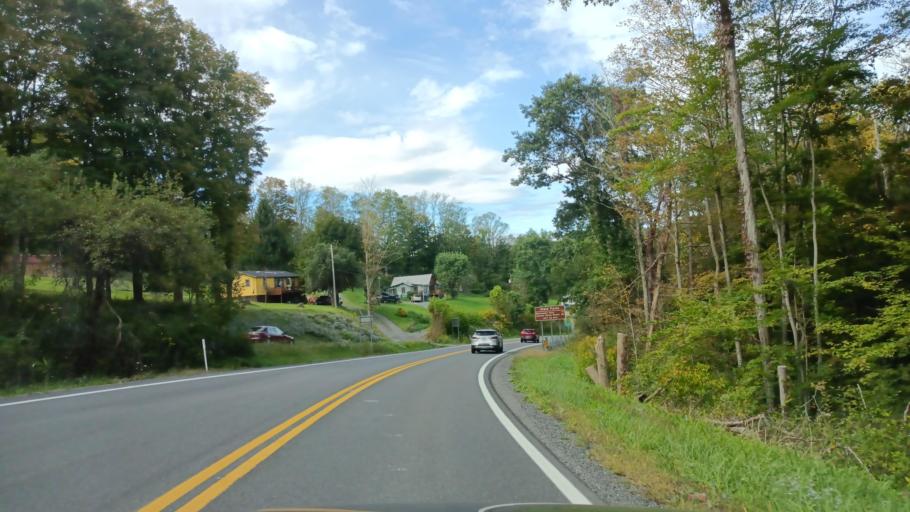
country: US
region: Maryland
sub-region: Garrett County
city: Mountain Lake Park
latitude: 39.2925
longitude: -79.3389
